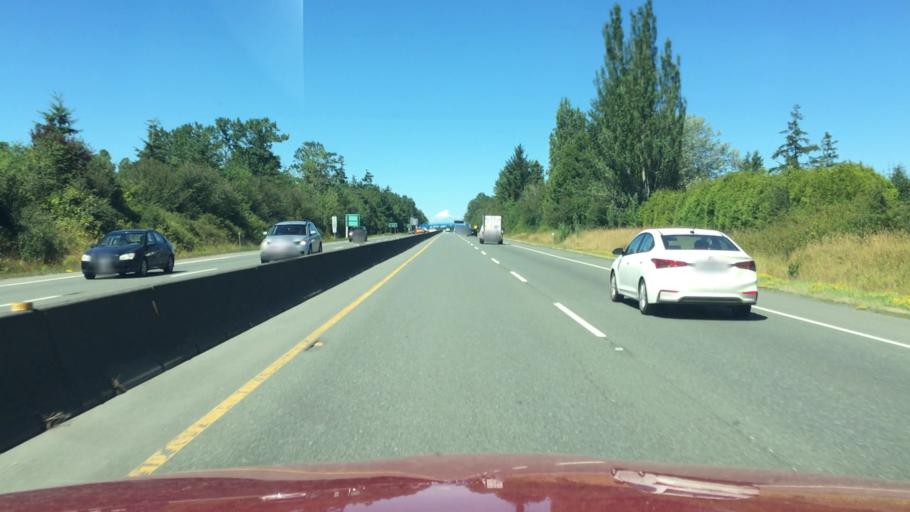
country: CA
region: British Columbia
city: North Saanich
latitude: 48.6357
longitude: -123.4096
